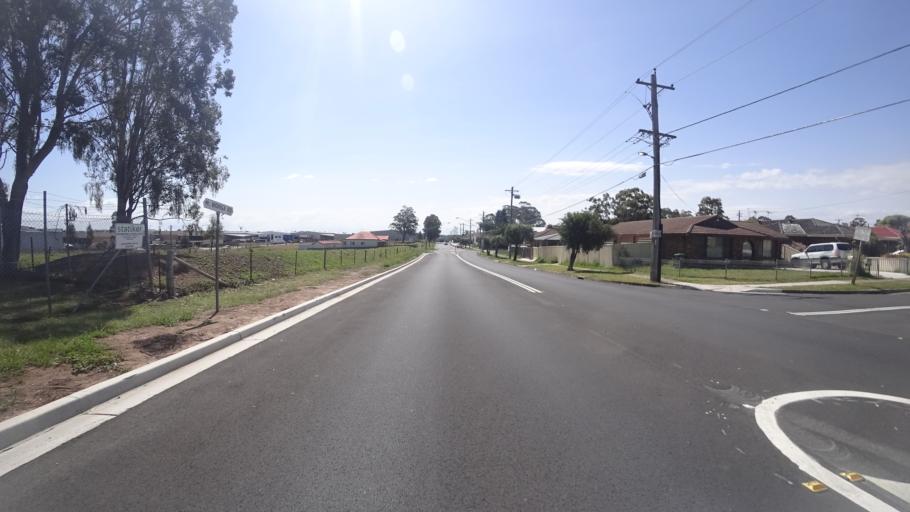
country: AU
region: New South Wales
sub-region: Liverpool
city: Miller
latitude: -33.9404
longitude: 150.8891
